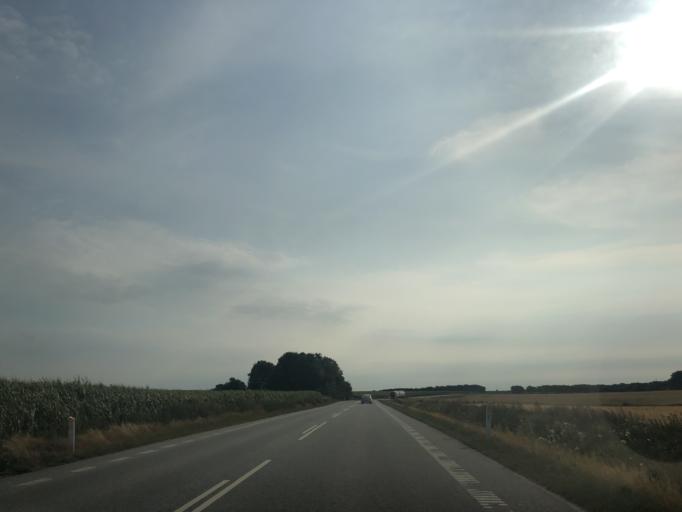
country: DK
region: Central Jutland
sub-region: Skive Kommune
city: Skive
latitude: 56.6304
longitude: 8.9115
